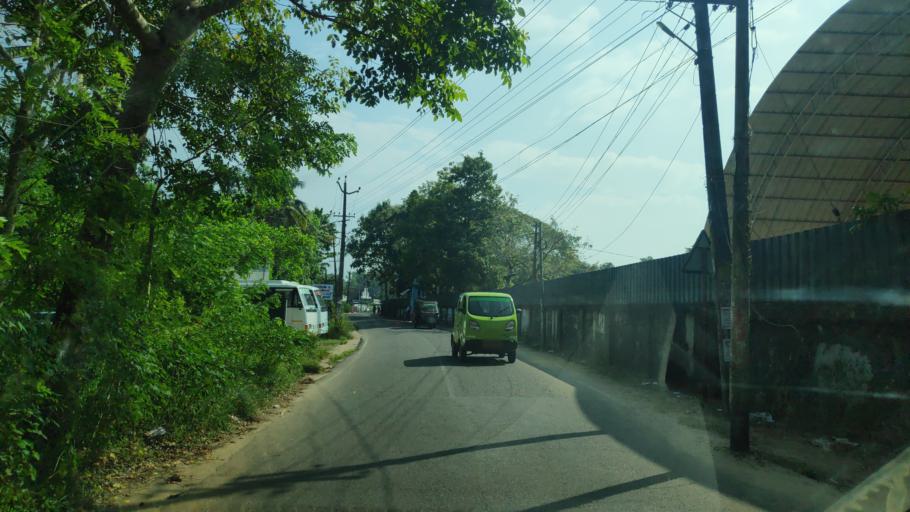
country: IN
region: Kerala
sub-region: Alappuzha
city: Alleppey
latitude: 9.5665
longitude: 76.3088
